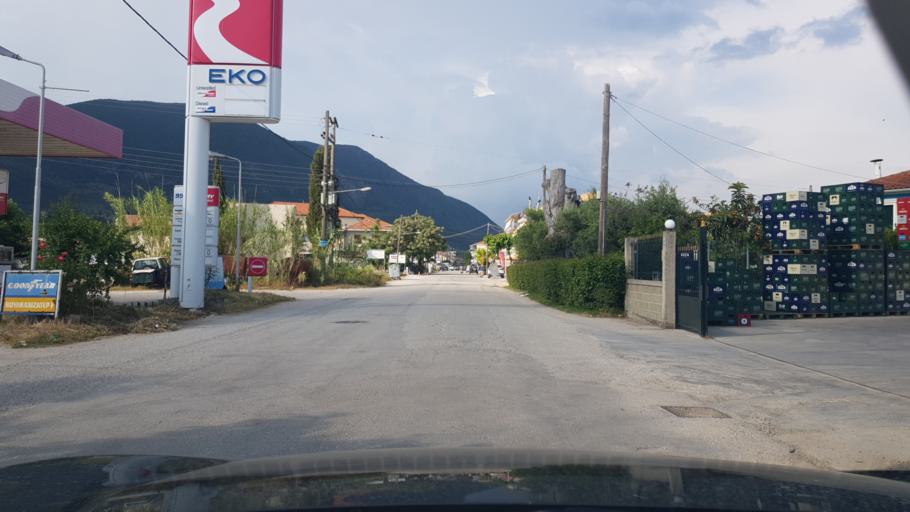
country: GR
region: Ionian Islands
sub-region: Lefkada
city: Nidri
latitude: 38.7021
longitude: 20.7063
